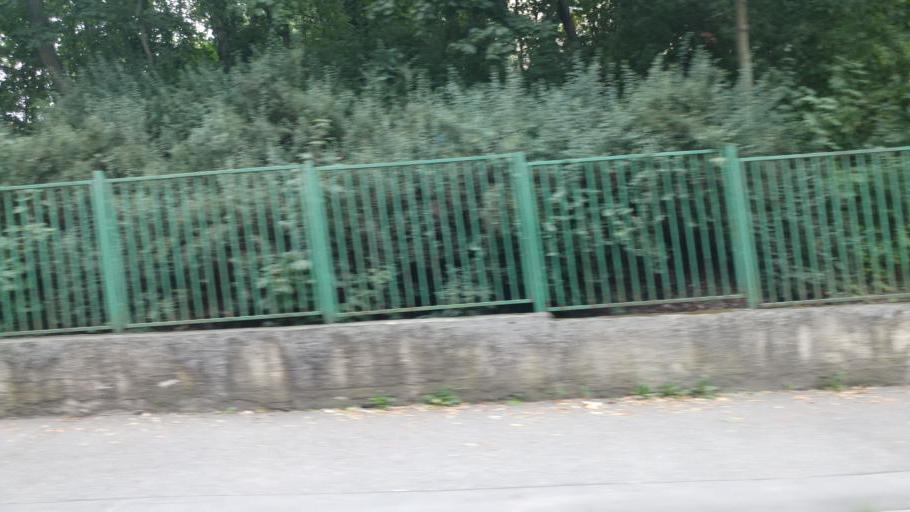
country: CZ
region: Praha
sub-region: Praha 9
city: Vysocany
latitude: 50.0917
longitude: 14.5134
